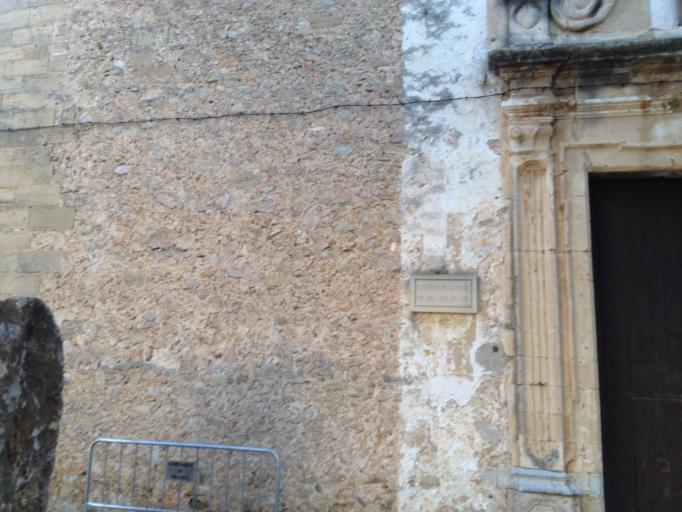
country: ES
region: Balearic Islands
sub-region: Illes Balears
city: Pollenca
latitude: 39.8756
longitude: 3.0164
